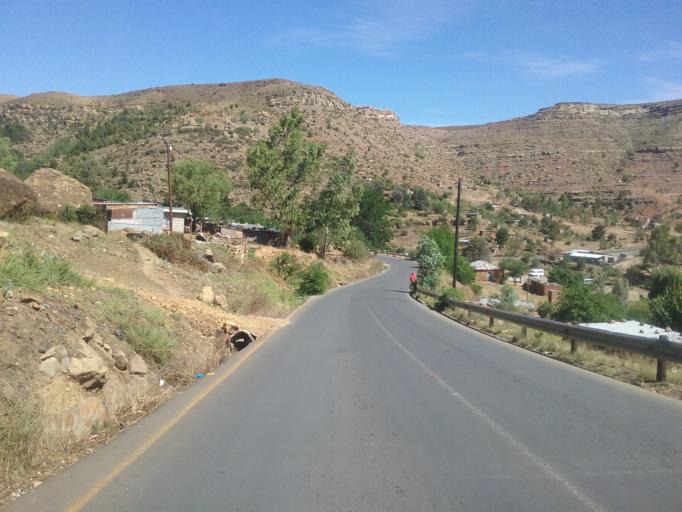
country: LS
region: Quthing
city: Quthing
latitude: -30.3998
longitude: 27.6930
